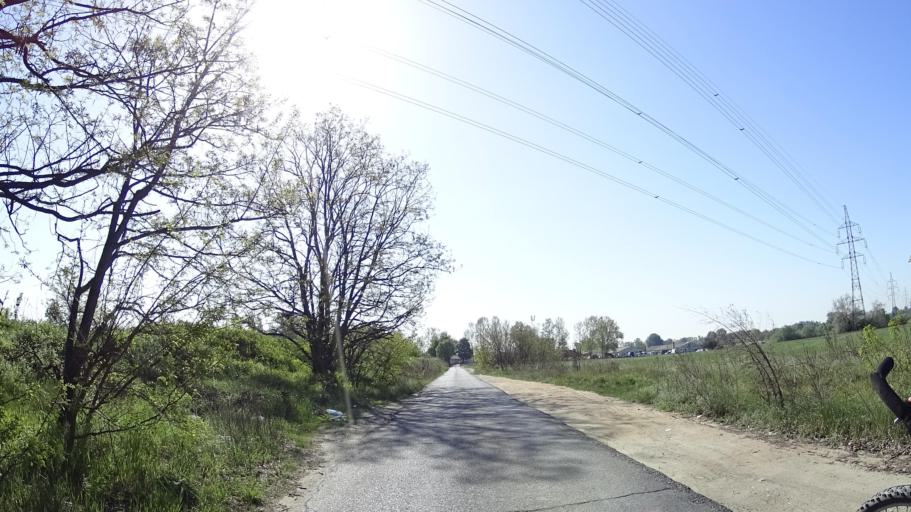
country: HU
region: Budapest
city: Budapest XXIII. keruelet
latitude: 47.4092
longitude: 19.1325
